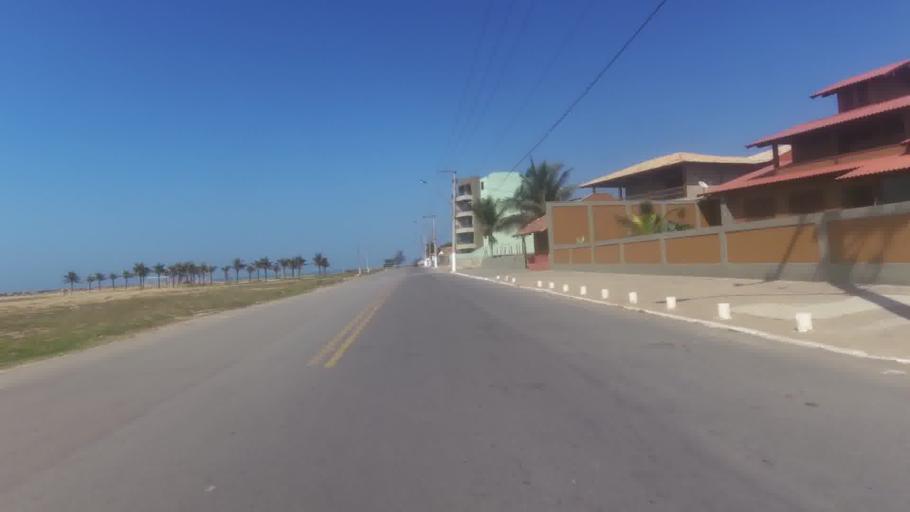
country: BR
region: Espirito Santo
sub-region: Marataizes
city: Marataizes
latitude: -21.0549
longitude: -40.8327
